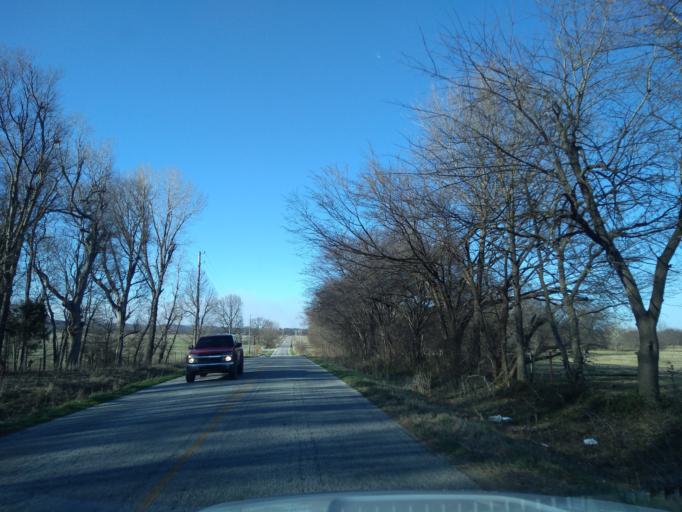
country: US
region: Arkansas
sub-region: Washington County
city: Lincoln
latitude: 36.0057
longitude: -94.3927
